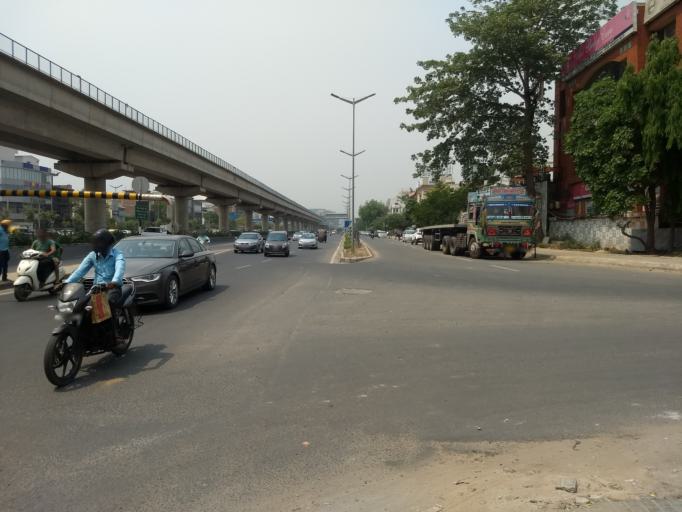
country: IN
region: Haryana
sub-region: Gurgaon
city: Gurgaon
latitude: 28.4720
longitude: 77.0942
